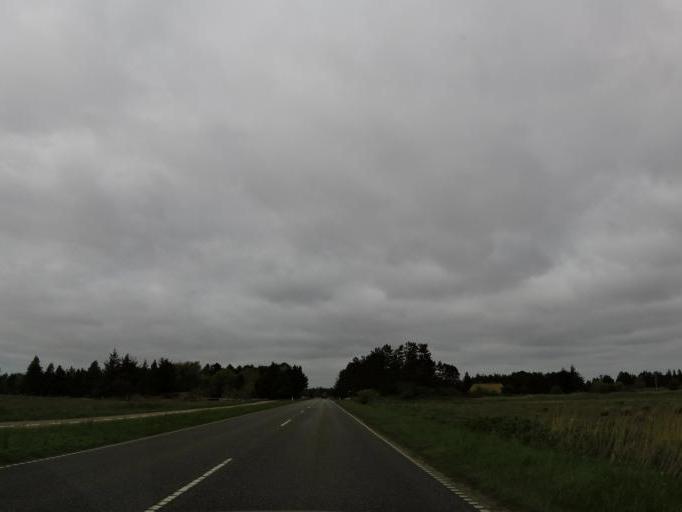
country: DE
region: Schleswig-Holstein
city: List
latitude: 55.1036
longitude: 8.5422
